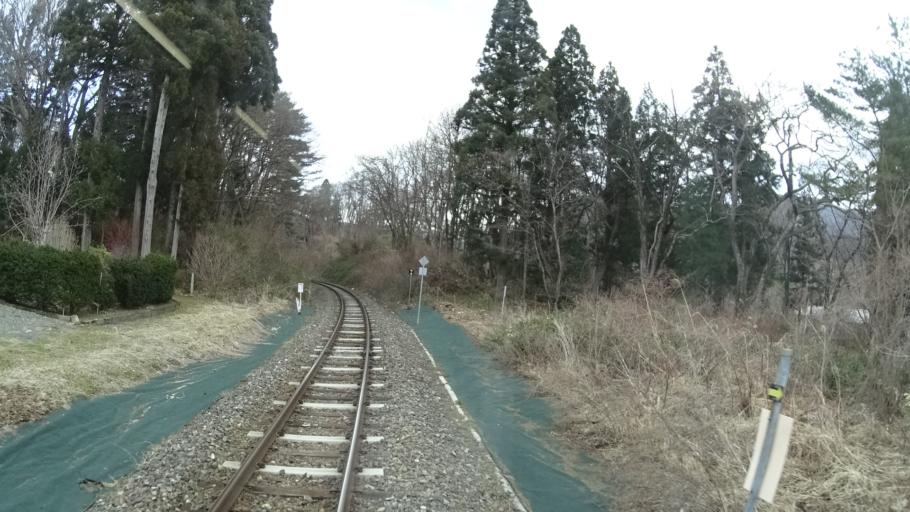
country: JP
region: Iwate
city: Tono
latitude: 39.3042
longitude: 141.3799
